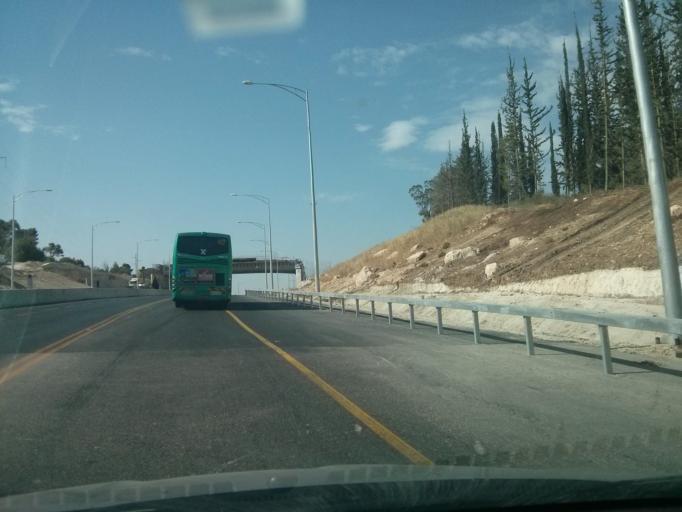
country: IL
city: Mevo horon
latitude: 31.7958
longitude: 35.0148
